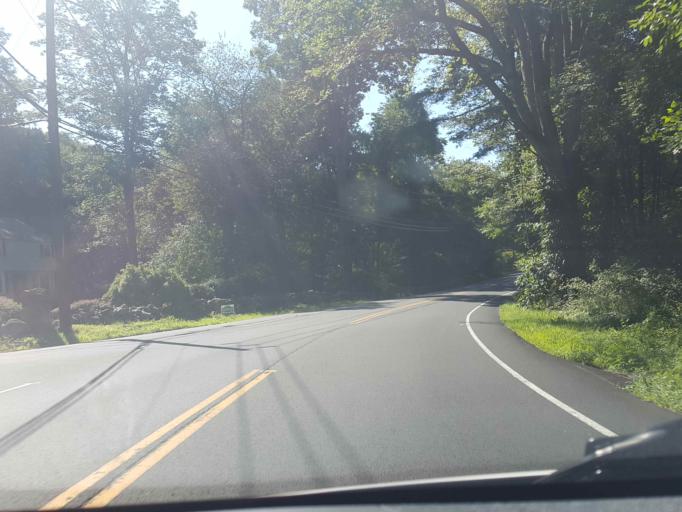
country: US
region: Connecticut
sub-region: New Haven County
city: Guilford
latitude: 41.3069
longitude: -72.6898
